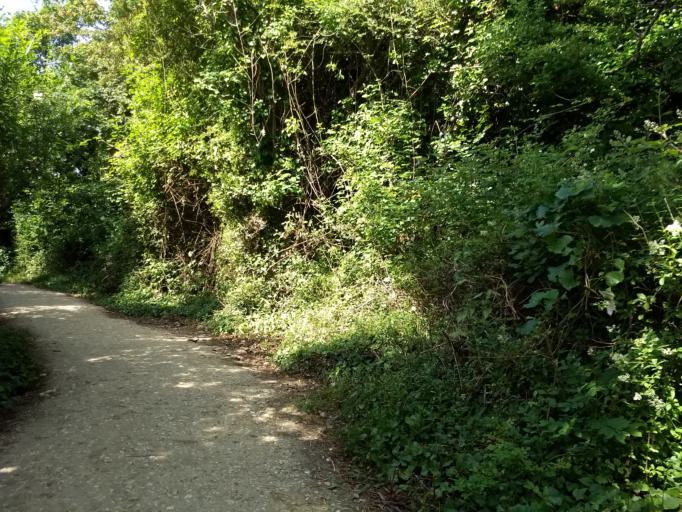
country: GB
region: England
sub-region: Isle of Wight
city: Bembridge
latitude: 50.6727
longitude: -1.0949
